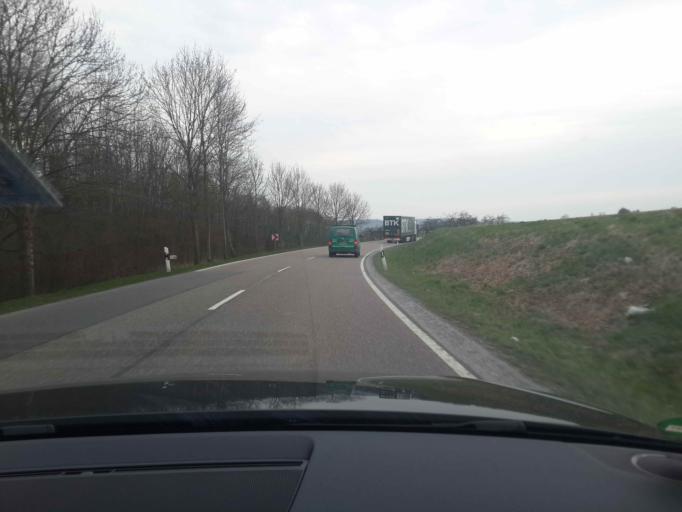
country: DE
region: Baden-Wuerttemberg
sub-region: Regierungsbezirk Stuttgart
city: Bretzfeld
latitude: 49.2279
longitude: 9.4343
